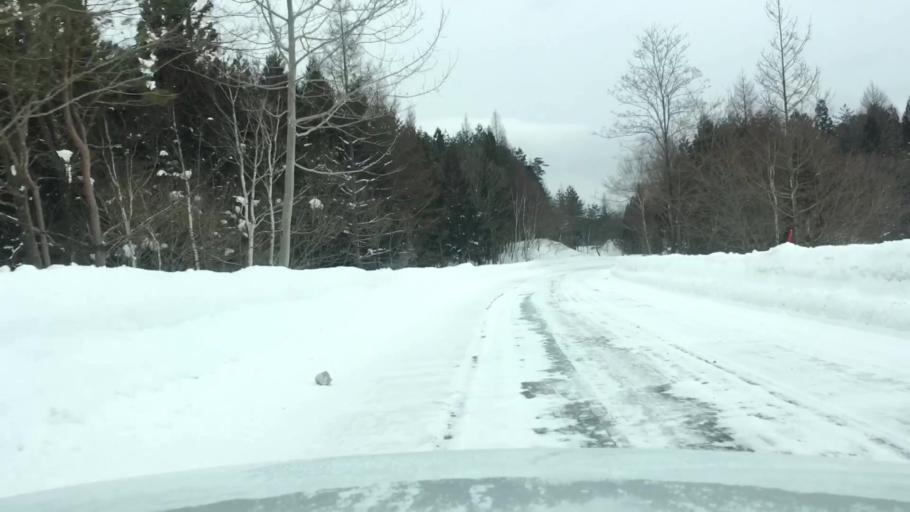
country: JP
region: Akita
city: Hanawa
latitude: 39.9890
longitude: 140.9972
